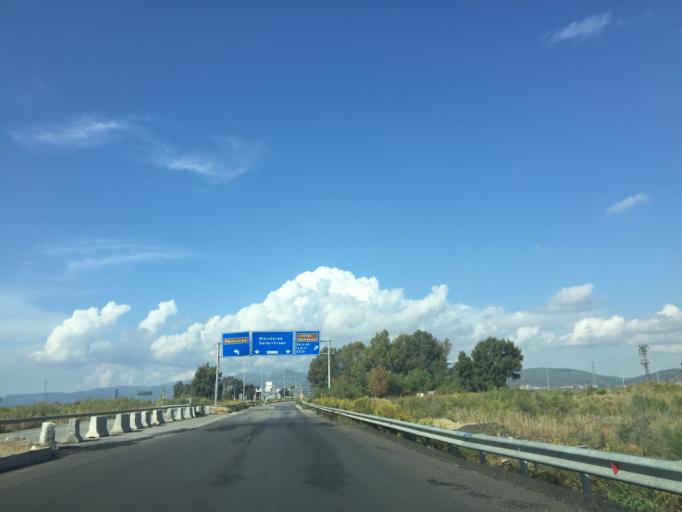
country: TR
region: Izmir
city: Selcuk
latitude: 37.9500
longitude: 27.3016
